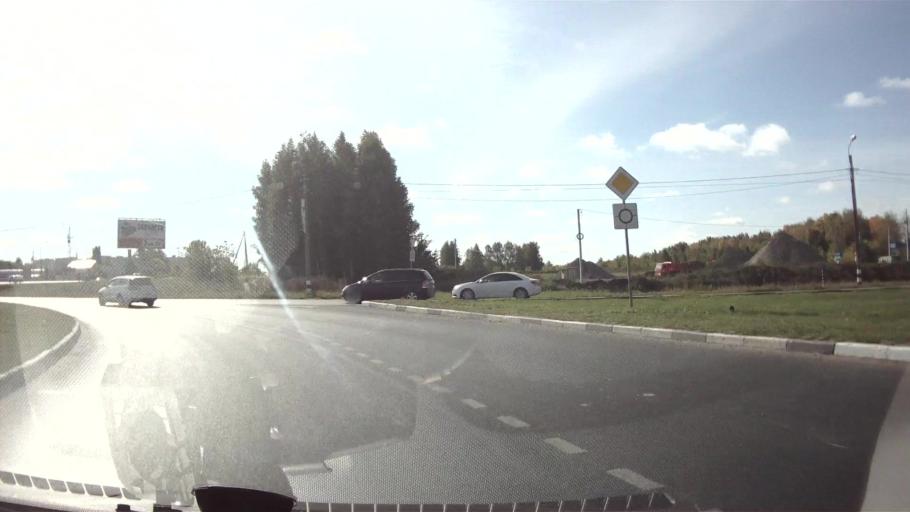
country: RU
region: Ulyanovsk
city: Isheyevka
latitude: 54.2908
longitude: 48.2540
